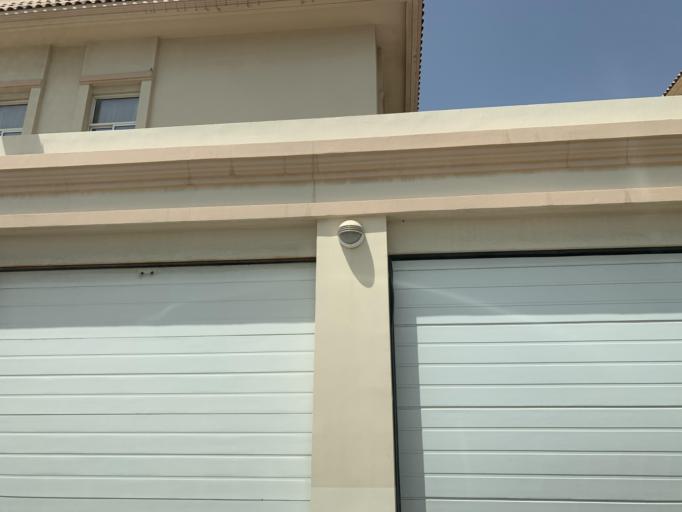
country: BH
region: Manama
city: Manama
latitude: 26.2001
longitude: 50.5671
